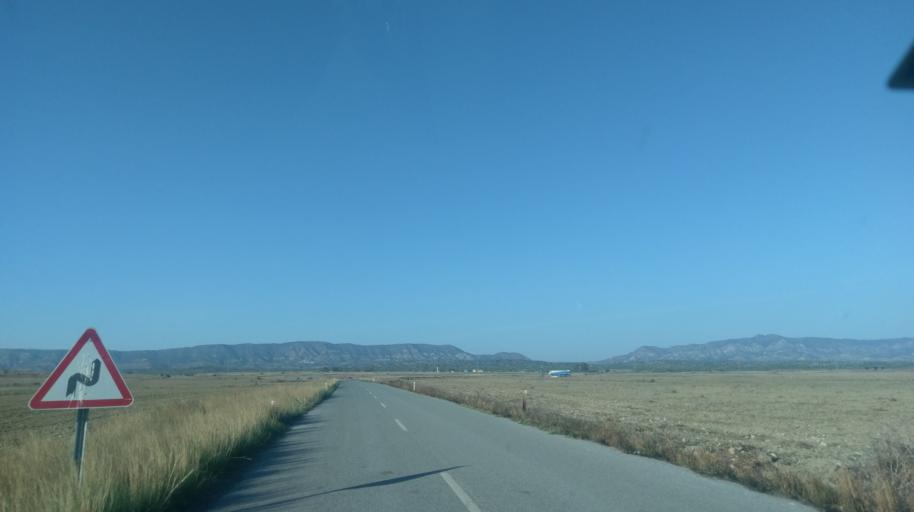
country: CY
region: Ammochostos
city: Lefkonoiko
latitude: 35.2645
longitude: 33.6868
